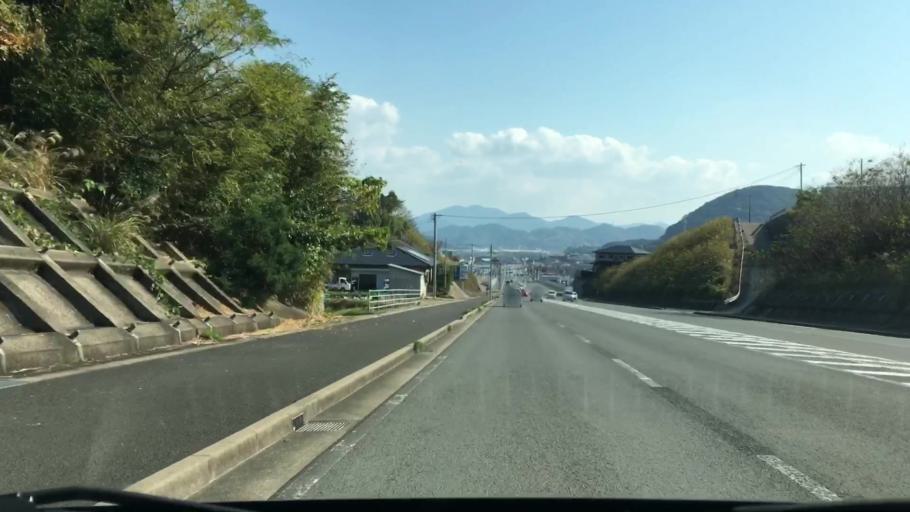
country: JP
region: Nagasaki
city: Togitsu
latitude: 32.8565
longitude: 129.8200
